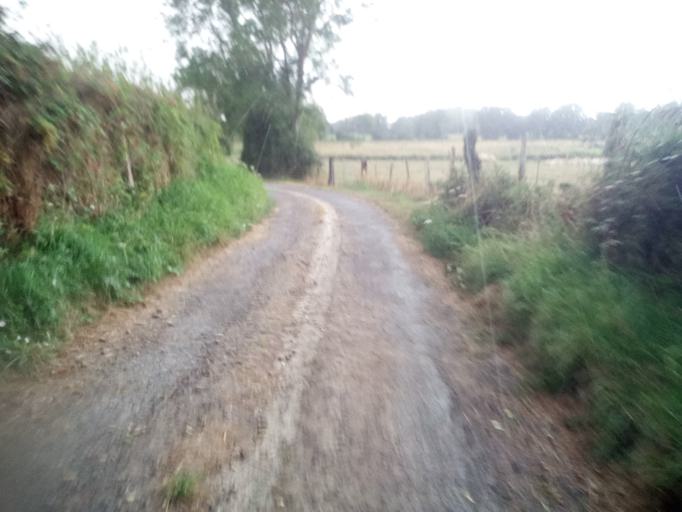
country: FR
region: Lower Normandy
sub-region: Departement du Calvados
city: Bavent
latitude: 49.2359
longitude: -0.1529
